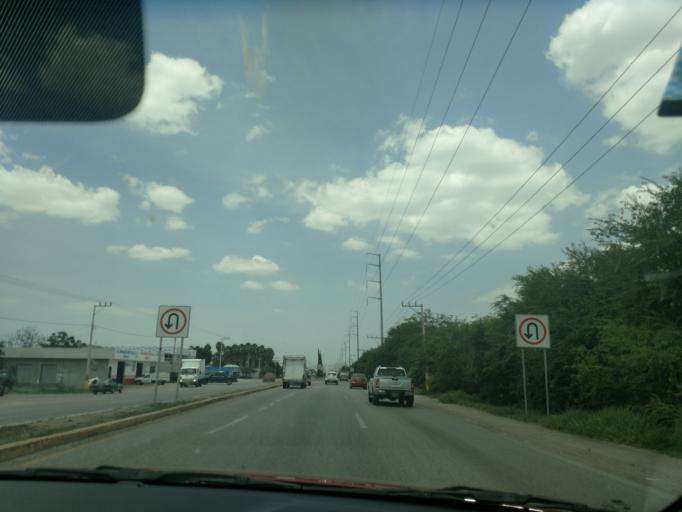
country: MX
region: San Luis Potosi
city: Rio Verde
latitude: 21.9227
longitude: -99.9874
